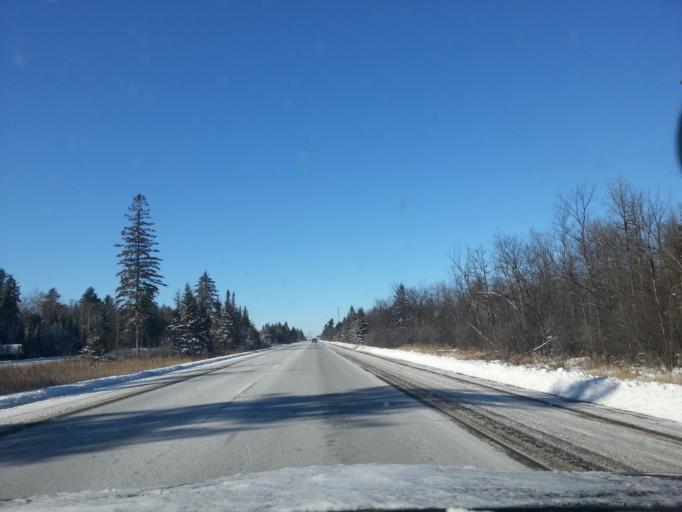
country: CA
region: Ontario
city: Carleton Place
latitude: 45.3182
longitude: -76.0836
